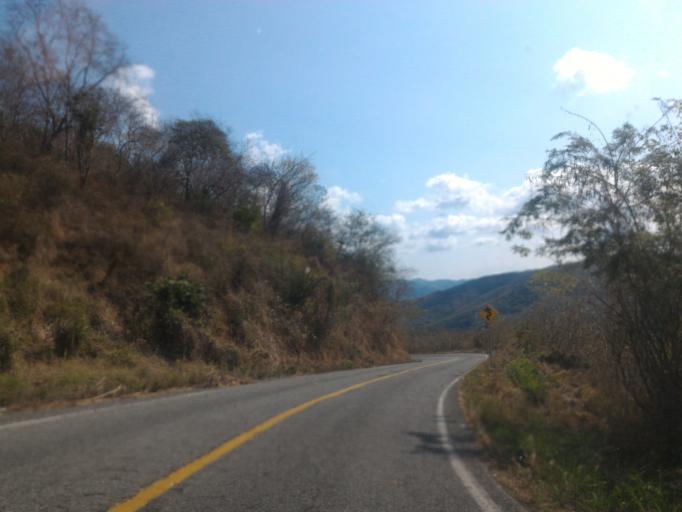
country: MX
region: Michoacan
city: Coahuayana Viejo
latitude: 18.4681
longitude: -103.5479
